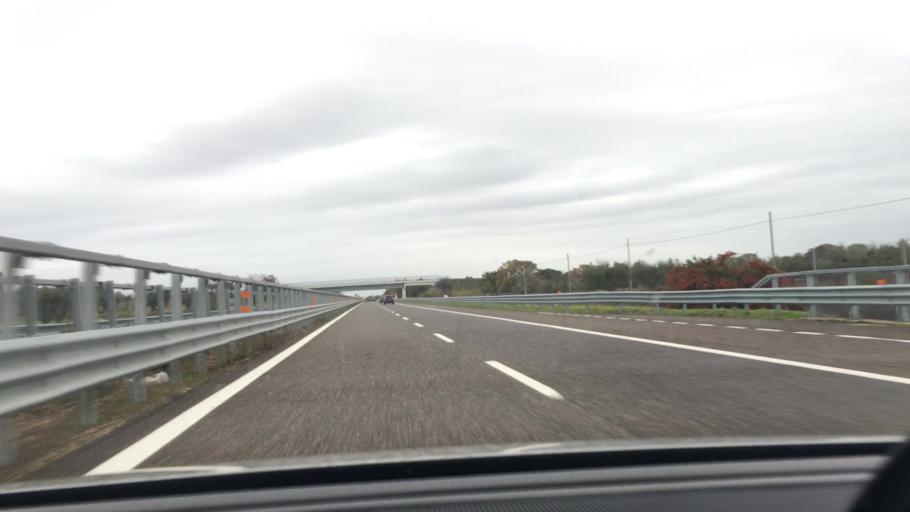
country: IT
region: Apulia
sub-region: Provincia di Bari
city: Gioia del Colle
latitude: 40.7468
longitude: 16.9150
